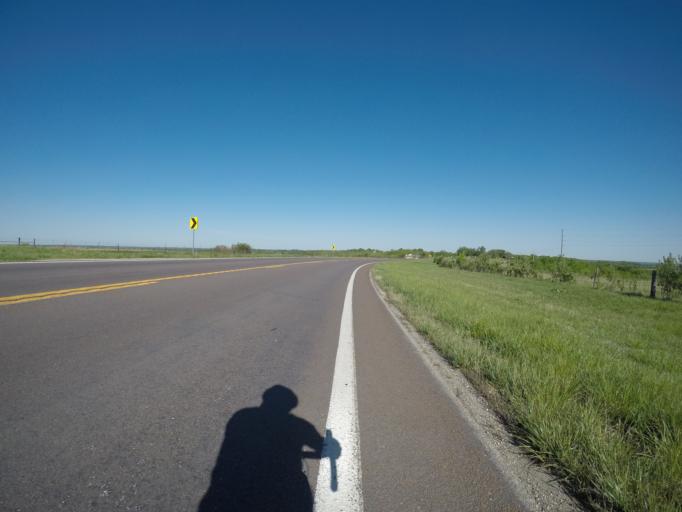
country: US
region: Kansas
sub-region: Douglas County
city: Lawrence
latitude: 38.9934
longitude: -95.3967
